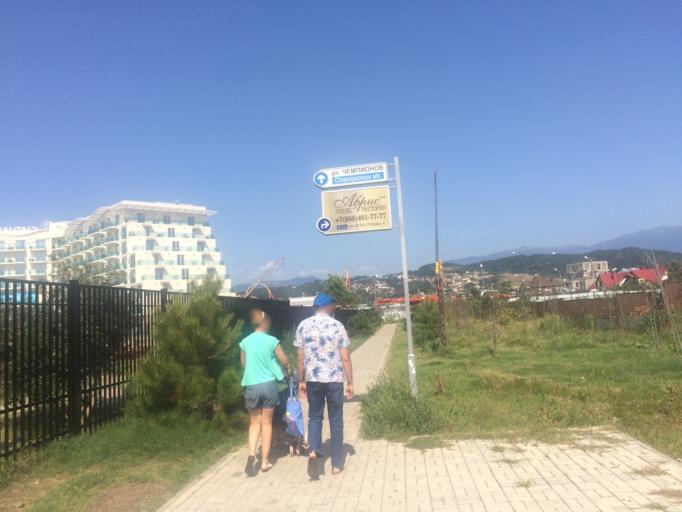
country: RU
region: Krasnodarskiy
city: Adler
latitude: 43.3987
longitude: 39.9654
